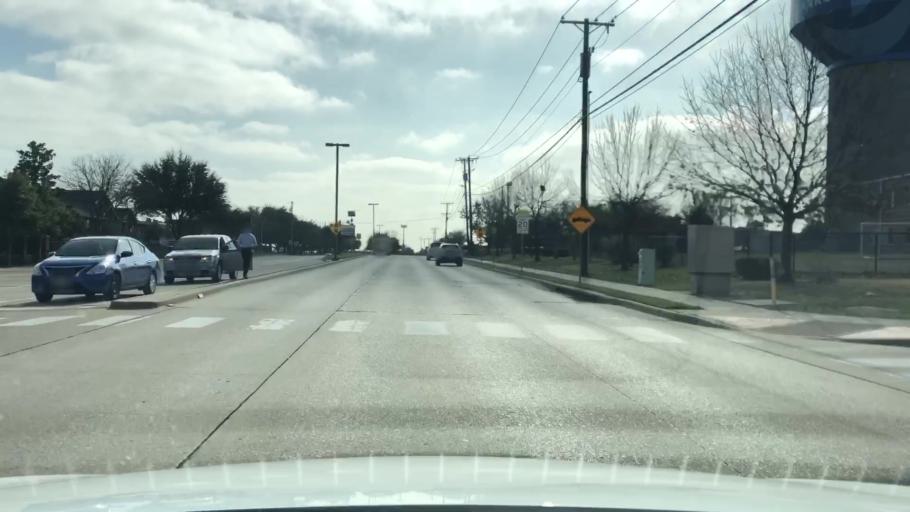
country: US
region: Texas
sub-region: Dallas County
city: Addison
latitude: 32.9742
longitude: -96.8558
